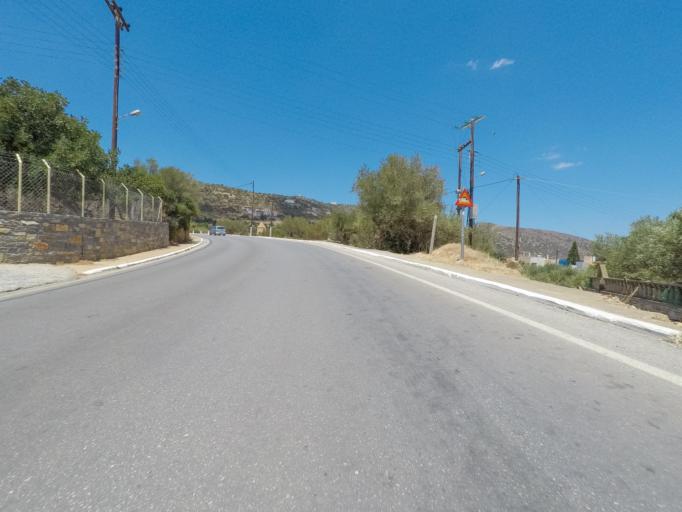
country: GR
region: Crete
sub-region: Nomos Lasithiou
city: Agios Nikolaos
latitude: 35.2158
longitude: 25.7124
